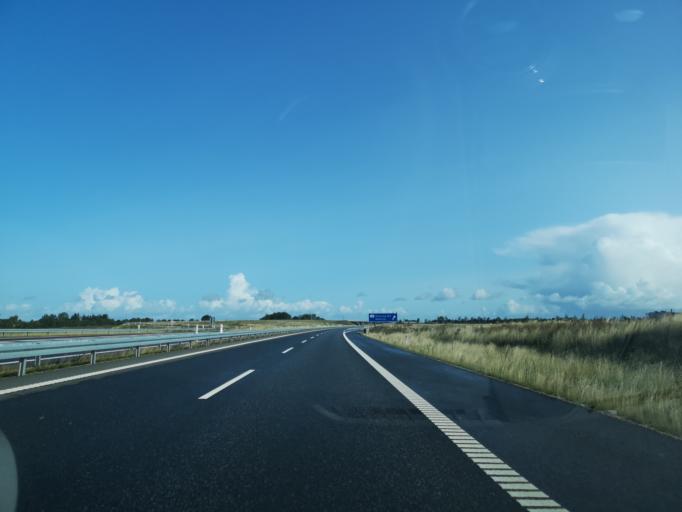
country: DK
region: Central Jutland
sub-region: Herning Kommune
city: Snejbjerg
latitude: 56.1483
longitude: 8.8711
